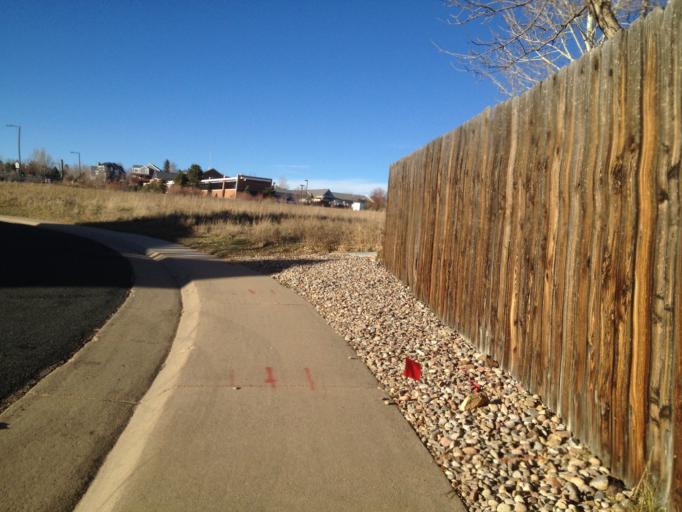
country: US
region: Colorado
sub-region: Boulder County
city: Superior
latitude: 39.9707
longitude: -105.1626
